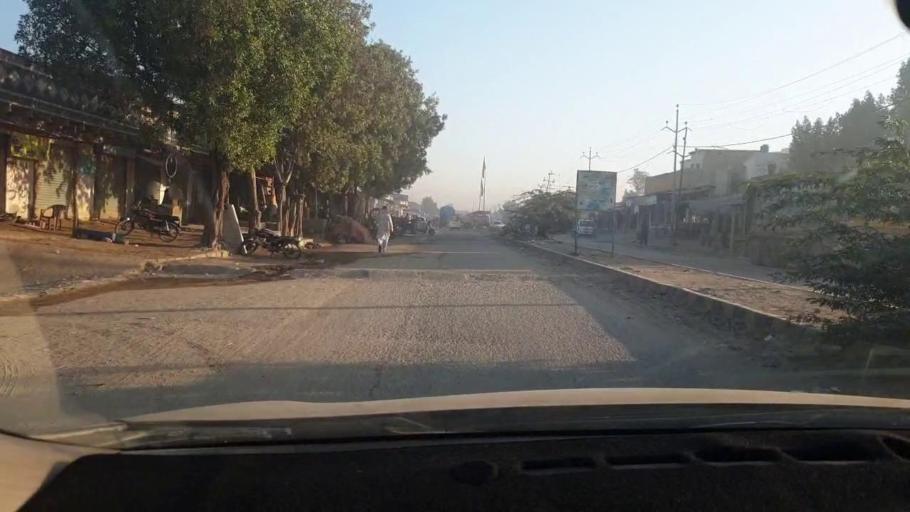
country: PK
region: Sindh
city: Malir Cantonment
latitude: 25.0118
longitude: 67.1675
